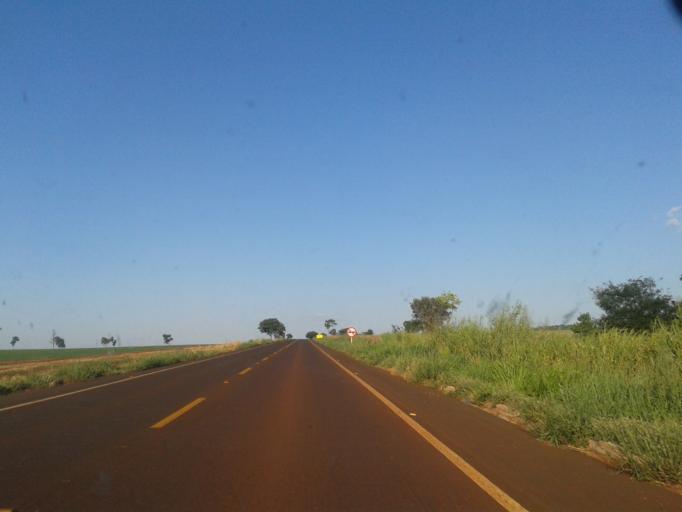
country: BR
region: Minas Gerais
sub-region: Capinopolis
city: Capinopolis
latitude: -18.7121
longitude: -49.8127
